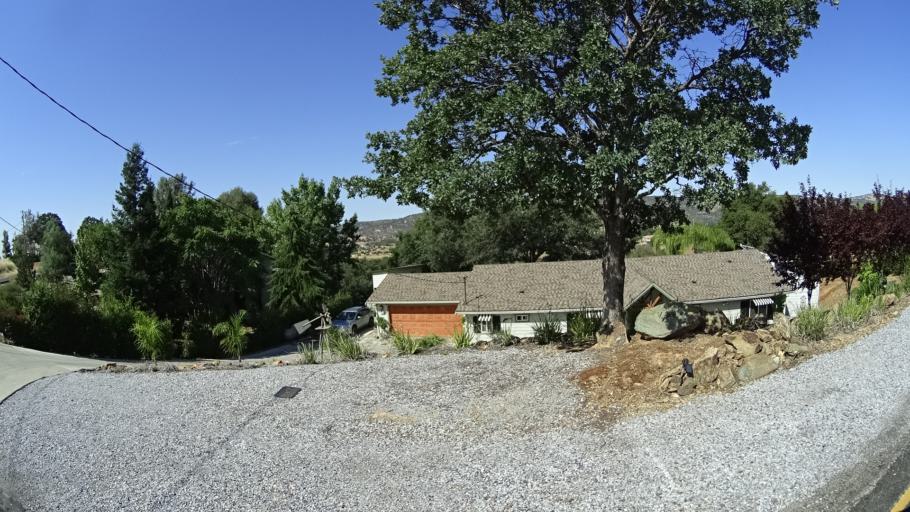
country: US
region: California
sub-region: Calaveras County
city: Copperopolis
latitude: 37.9258
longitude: -120.6335
